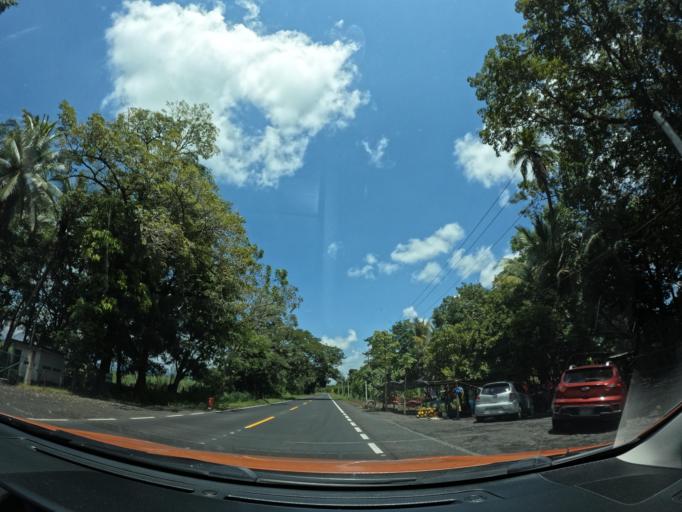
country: GT
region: Escuintla
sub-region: Municipio de Masagua
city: Masagua
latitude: 14.1732
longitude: -90.8727
